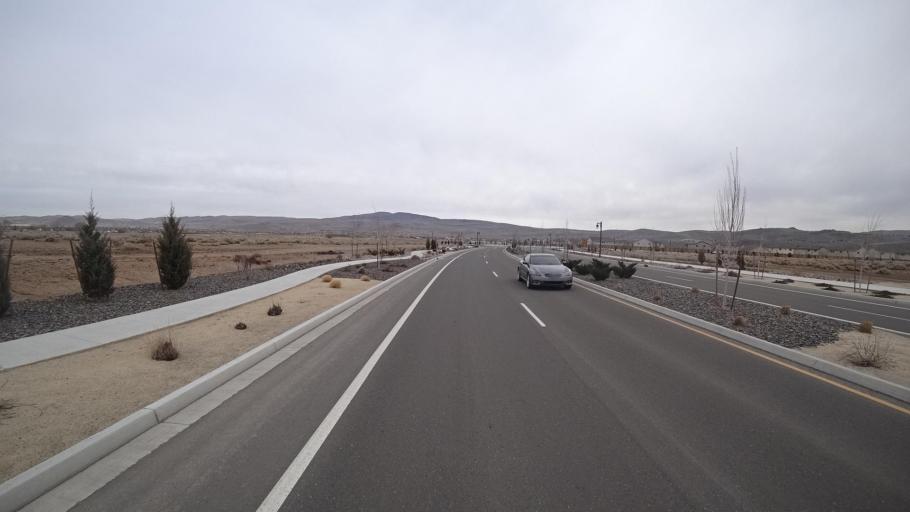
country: US
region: Nevada
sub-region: Washoe County
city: Spanish Springs
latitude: 39.6155
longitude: -119.7204
